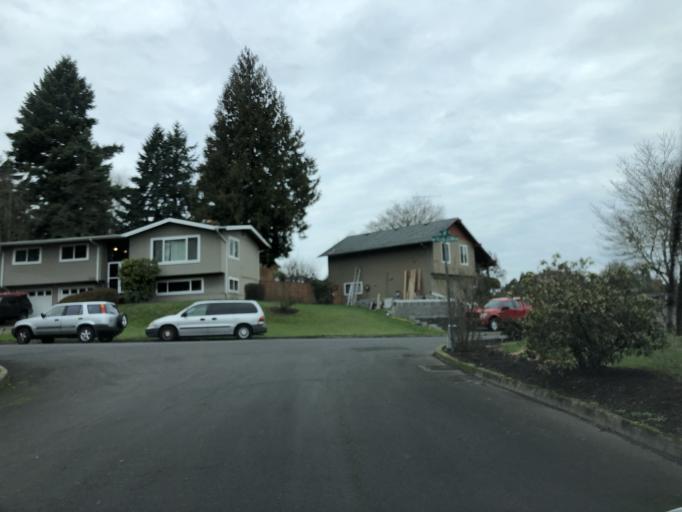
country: US
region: Oregon
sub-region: Washington County
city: Tigard
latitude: 45.4232
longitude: -122.7735
